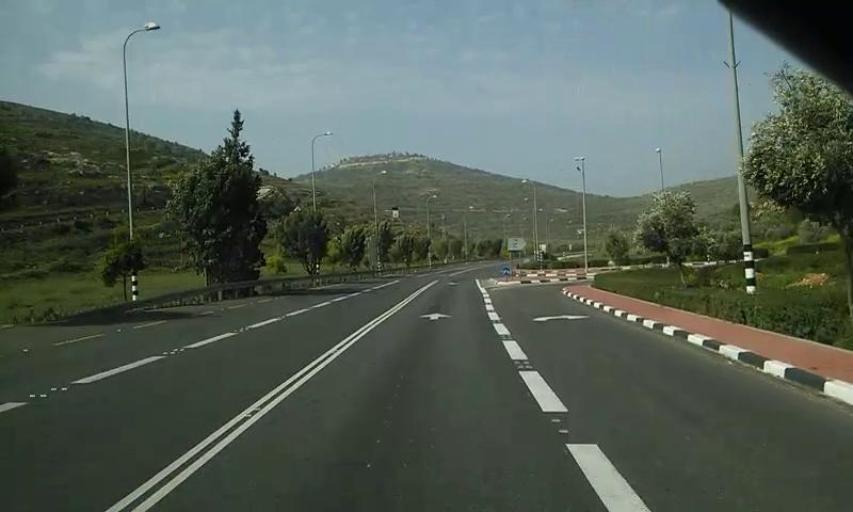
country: PS
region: West Bank
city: Al Lubban ash Sharqiyah
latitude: 32.0625
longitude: 35.2552
